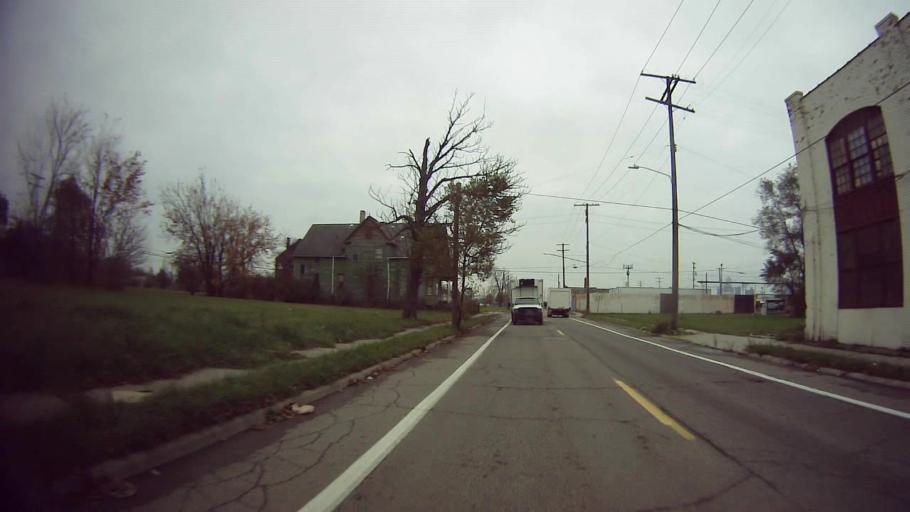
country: US
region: Michigan
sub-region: Wayne County
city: Detroit
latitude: 42.3563
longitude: -83.0390
